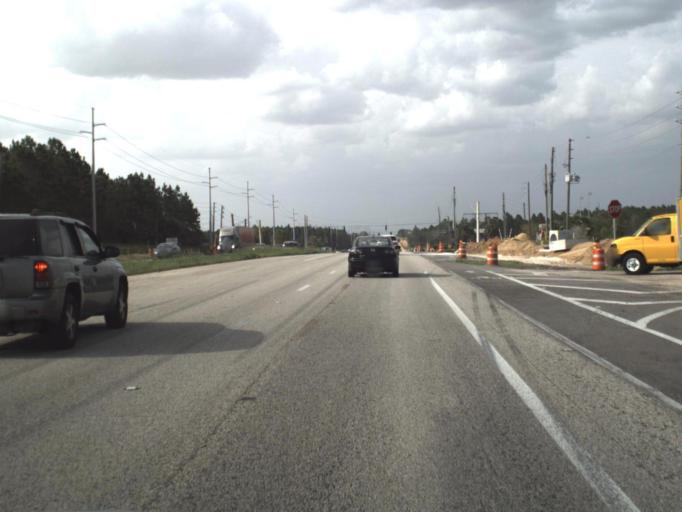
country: US
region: Florida
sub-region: Lake County
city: Four Corners
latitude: 28.3080
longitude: -81.6671
